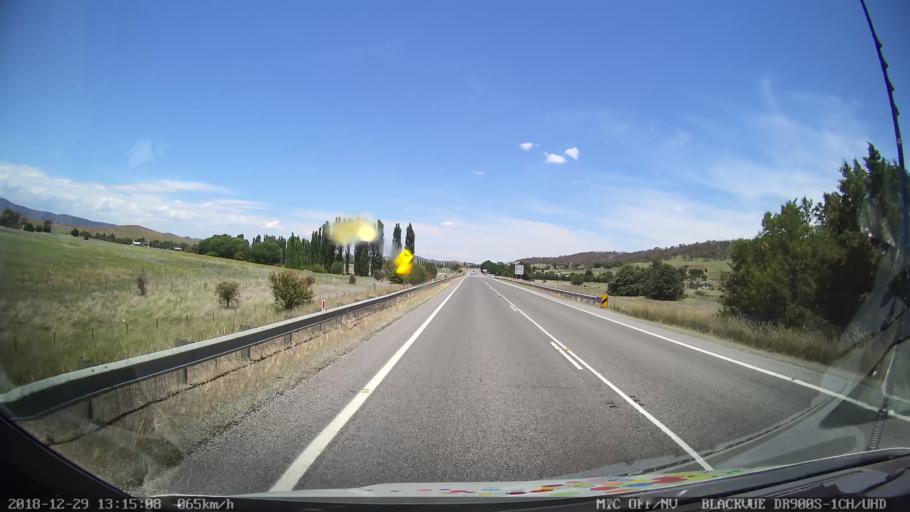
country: AU
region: Australian Capital Territory
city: Macarthur
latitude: -35.7051
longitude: 149.1583
